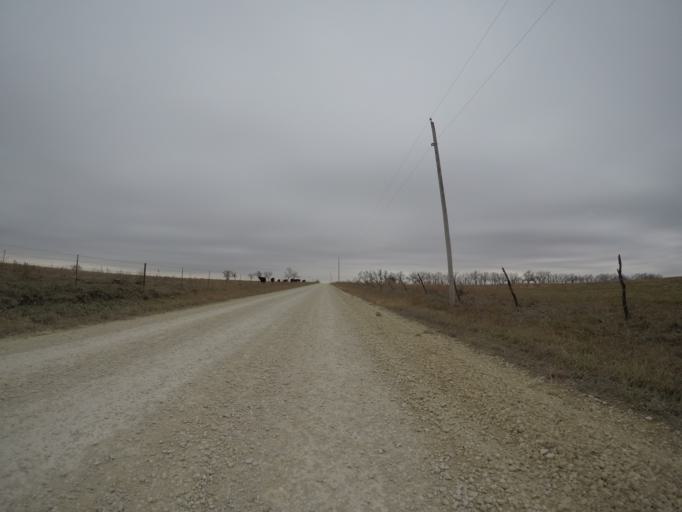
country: US
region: Kansas
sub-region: Wabaunsee County
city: Alma
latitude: 38.8282
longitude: -96.1133
